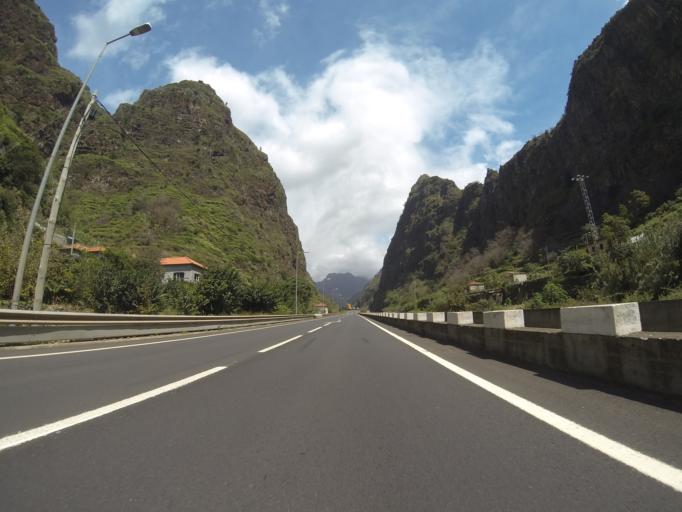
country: PT
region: Madeira
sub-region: Ribeira Brava
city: Campanario
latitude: 32.7005
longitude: -17.0413
